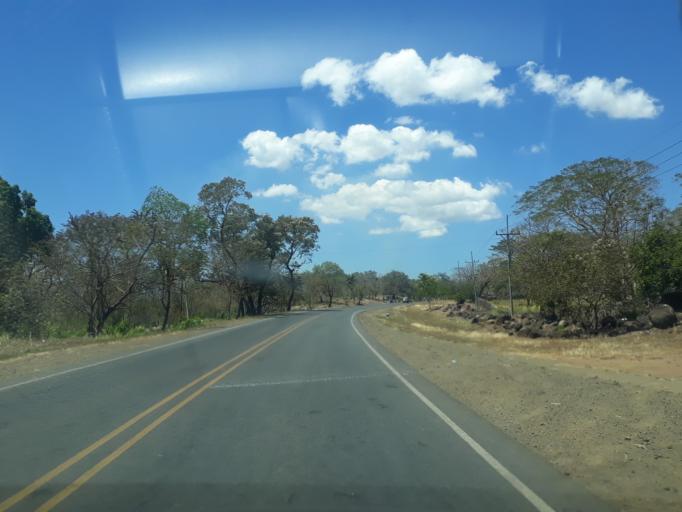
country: CR
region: Guanacaste
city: Liberia
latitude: 10.6691
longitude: -85.4819
